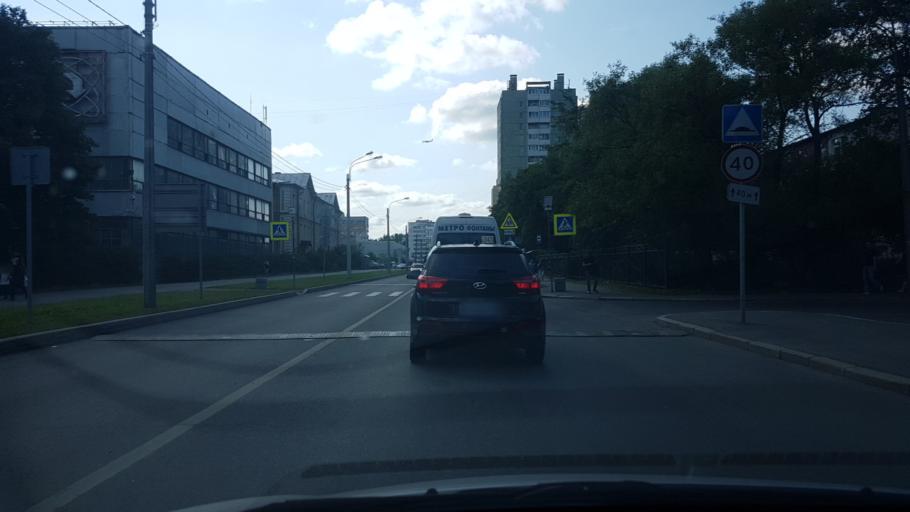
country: RU
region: St.-Petersburg
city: Sosnovaya Polyana
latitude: 59.8450
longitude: 30.1303
